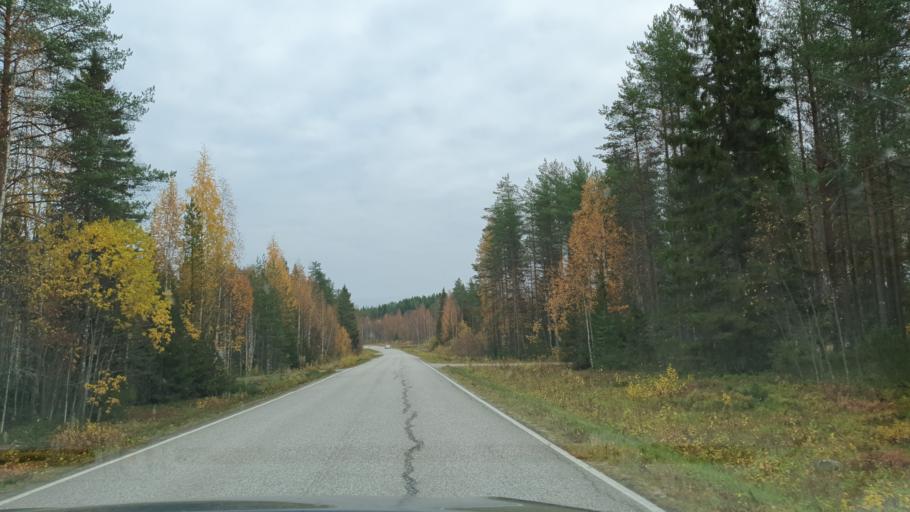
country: FI
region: Kainuu
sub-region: Kajaani
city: Ristijaervi
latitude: 64.4561
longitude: 28.3344
